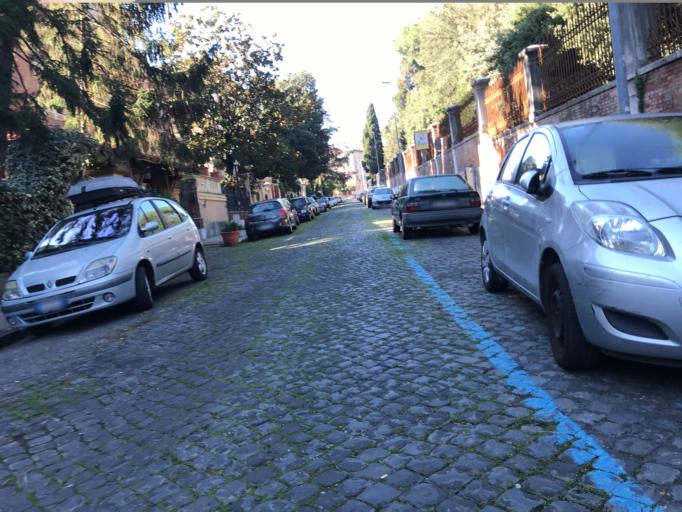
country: IT
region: Latium
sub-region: Citta metropolitana di Roma Capitale
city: Rome
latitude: 41.9144
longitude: 12.5009
